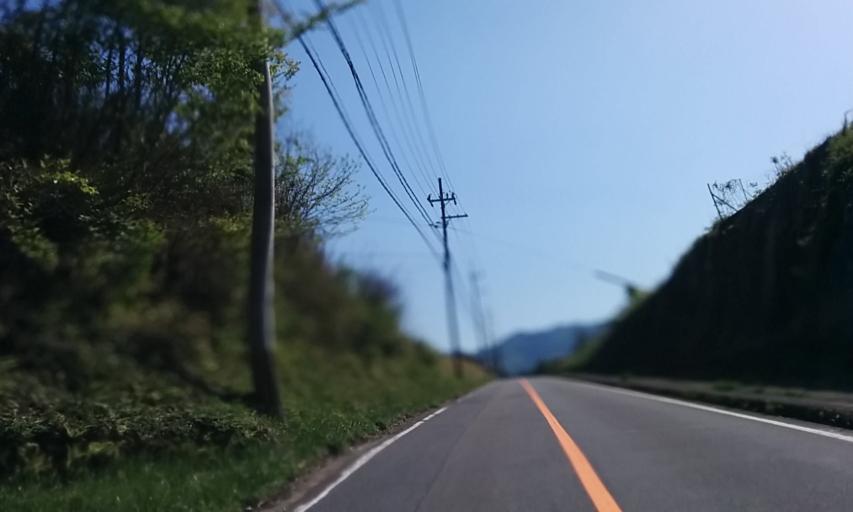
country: JP
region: Kyoto
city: Maizuru
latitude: 35.2763
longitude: 135.5072
